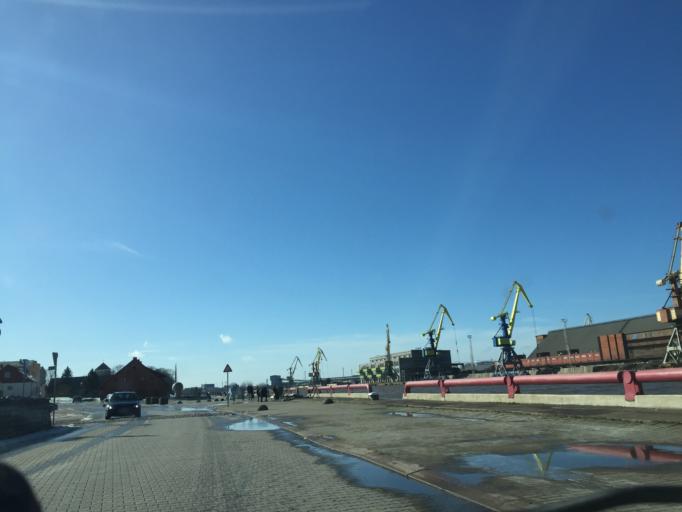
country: LV
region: Ventspils
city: Ventspils
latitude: 57.3983
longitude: 21.5662
